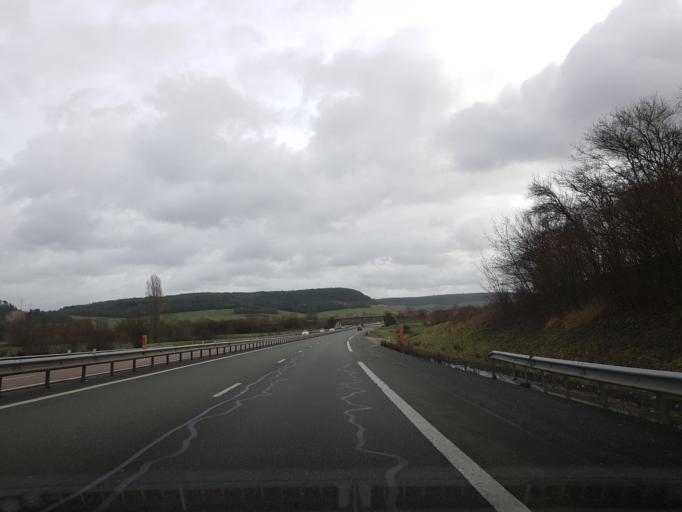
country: FR
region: Champagne-Ardenne
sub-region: Departement de la Haute-Marne
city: Chateauvillain
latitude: 48.0768
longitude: 4.8856
